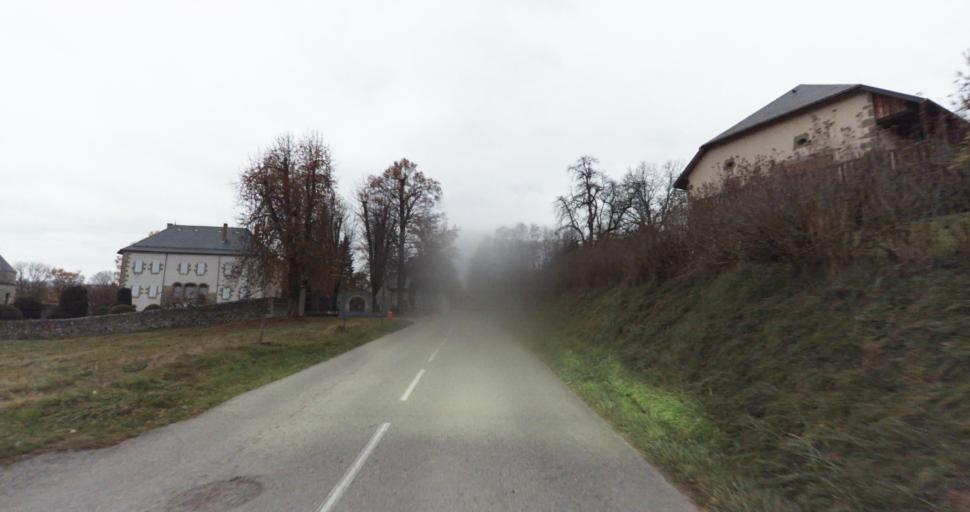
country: FR
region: Rhone-Alpes
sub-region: Departement de la Haute-Savoie
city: Alby-sur-Cheran
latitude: 45.8348
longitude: 6.0112
